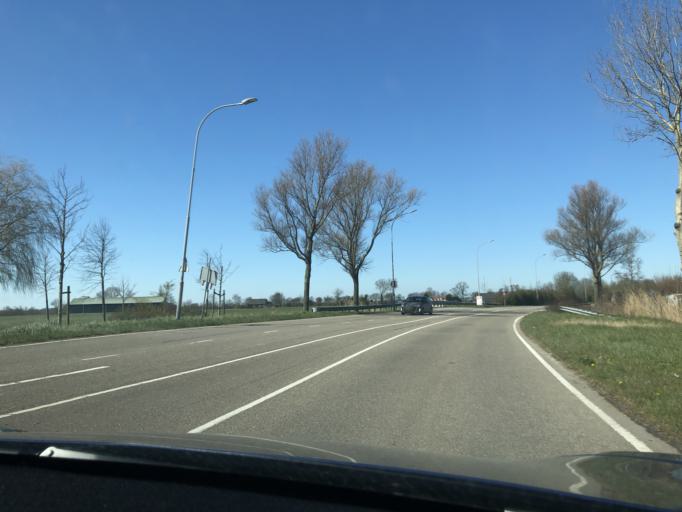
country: NL
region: Zeeland
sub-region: Gemeente Middelburg
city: Middelburg
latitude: 51.4818
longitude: 3.5965
